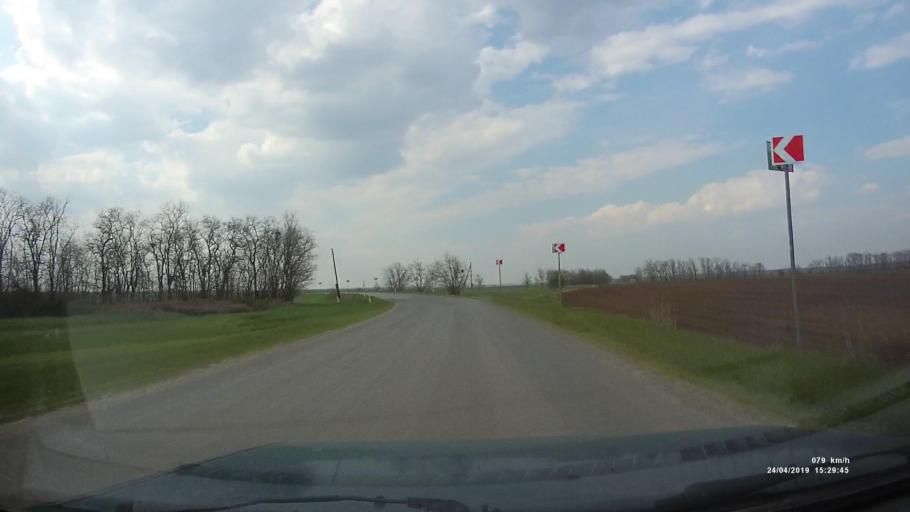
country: RU
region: Rostov
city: Remontnoye
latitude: 46.5974
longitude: 43.0165
